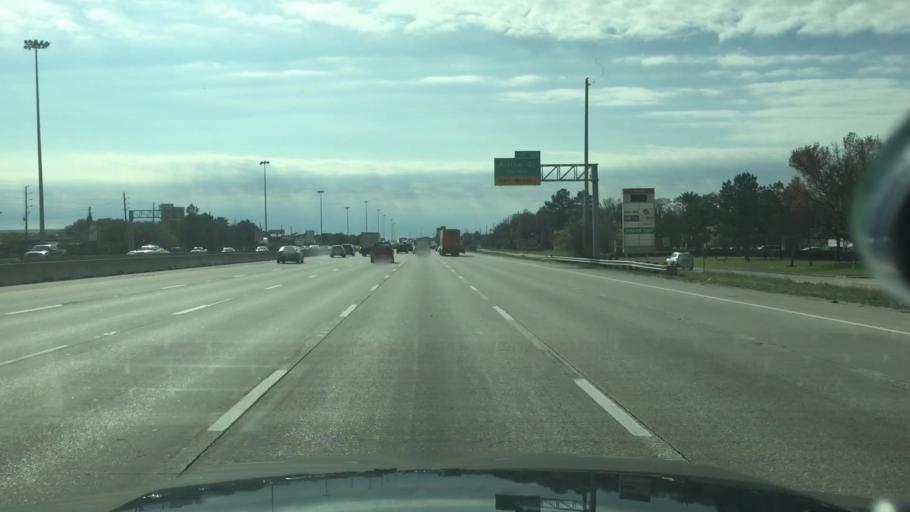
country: US
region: Texas
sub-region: Harris County
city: Aldine
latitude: 29.9906
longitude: -95.4244
